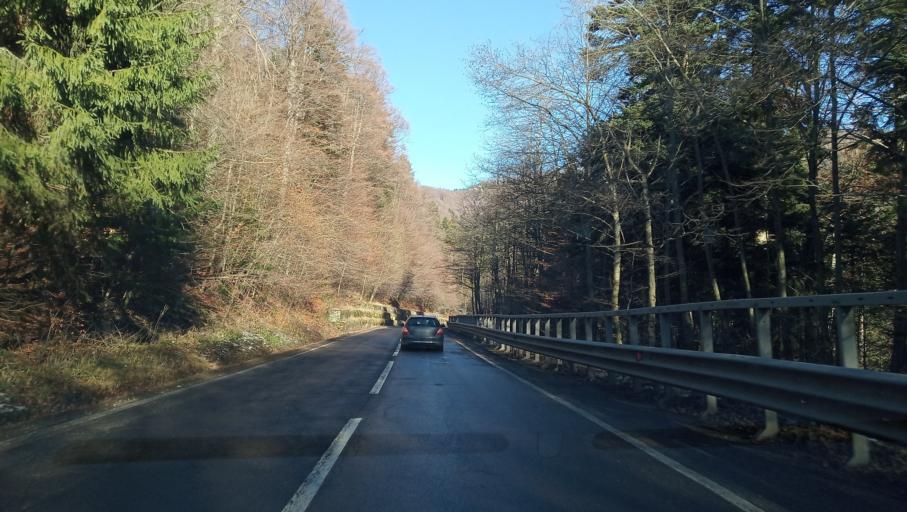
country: RO
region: Brasov
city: Crivina
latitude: 45.4708
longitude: 25.9322
